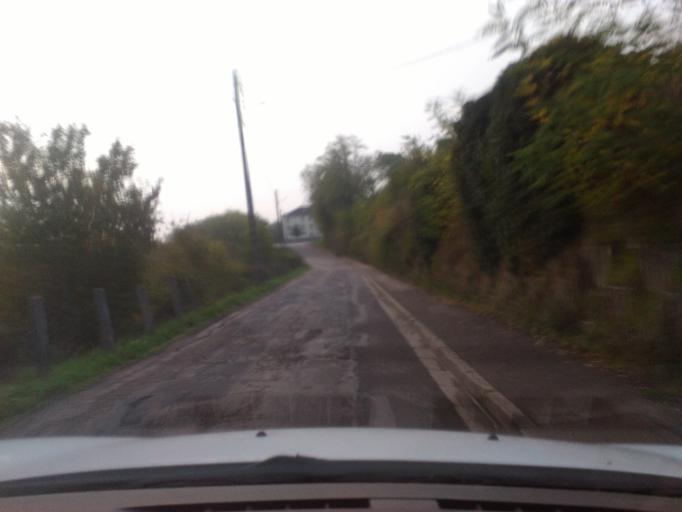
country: FR
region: Lorraine
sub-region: Departement des Vosges
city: Mirecourt
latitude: 48.3005
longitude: 6.1281
